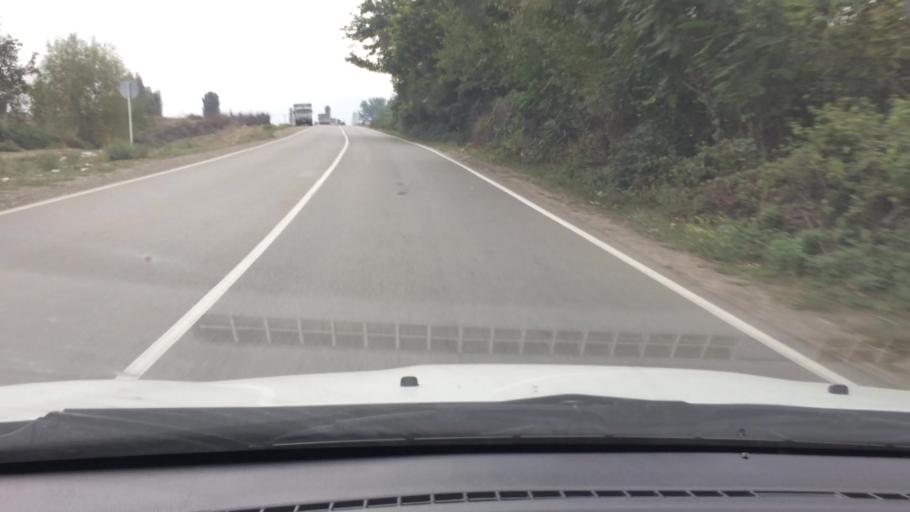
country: AM
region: Tavush
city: Bagratashen
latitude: 41.2340
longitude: 44.8116
